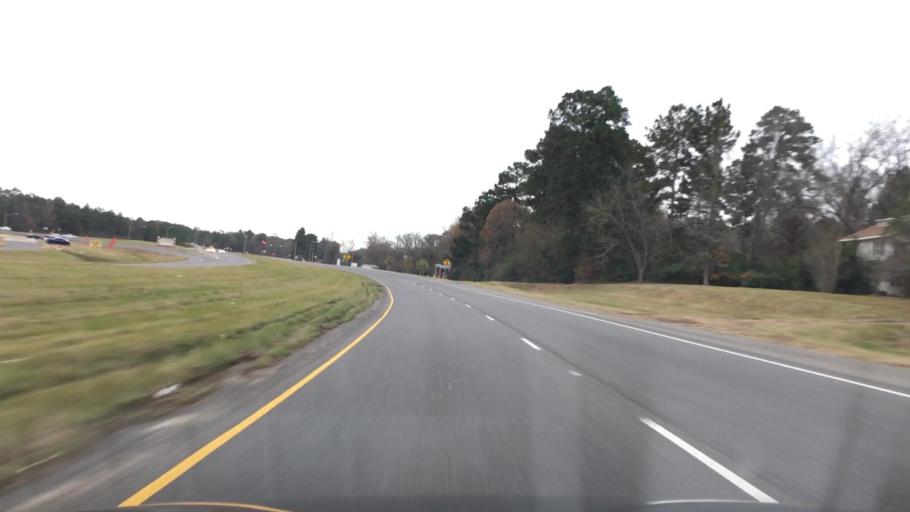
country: US
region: Louisiana
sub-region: Vernon Parish
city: New Llano
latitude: 31.0697
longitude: -93.2743
